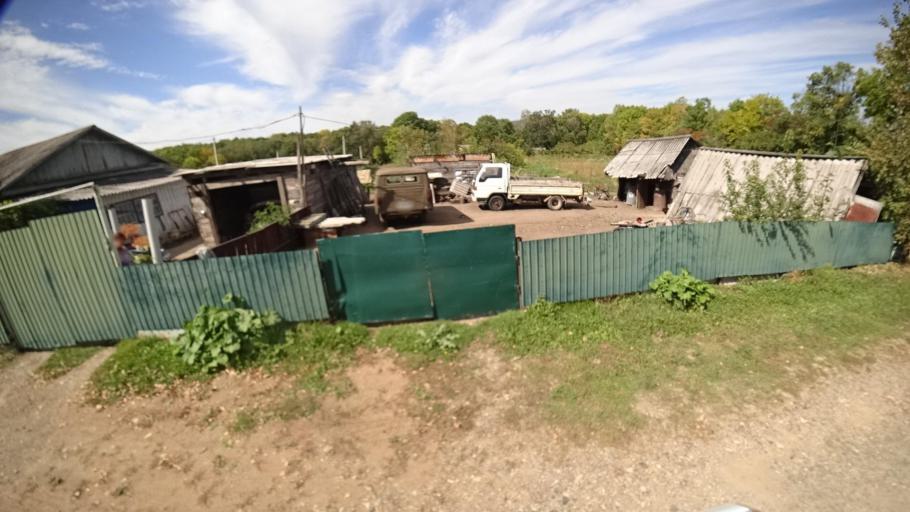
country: RU
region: Primorskiy
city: Yakovlevka
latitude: 44.7066
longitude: 133.6418
